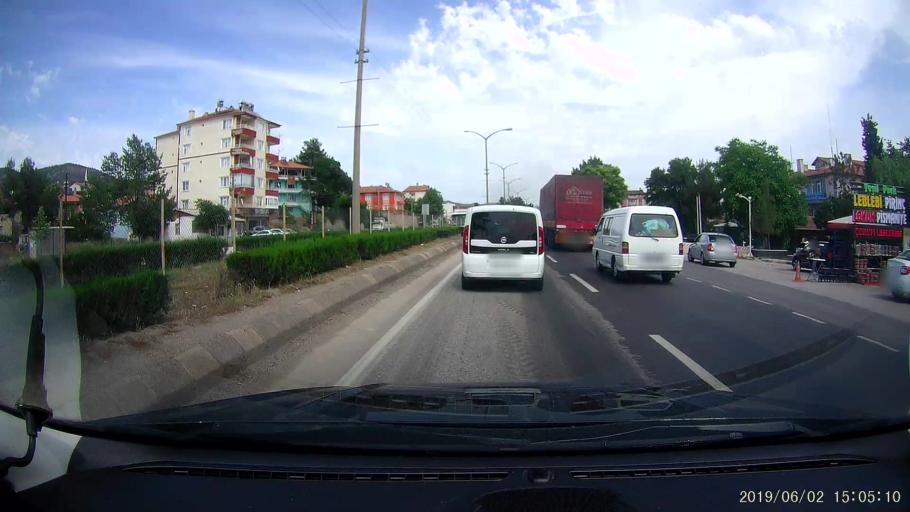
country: TR
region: Corum
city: Osmancik
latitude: 40.9797
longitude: 34.7991
